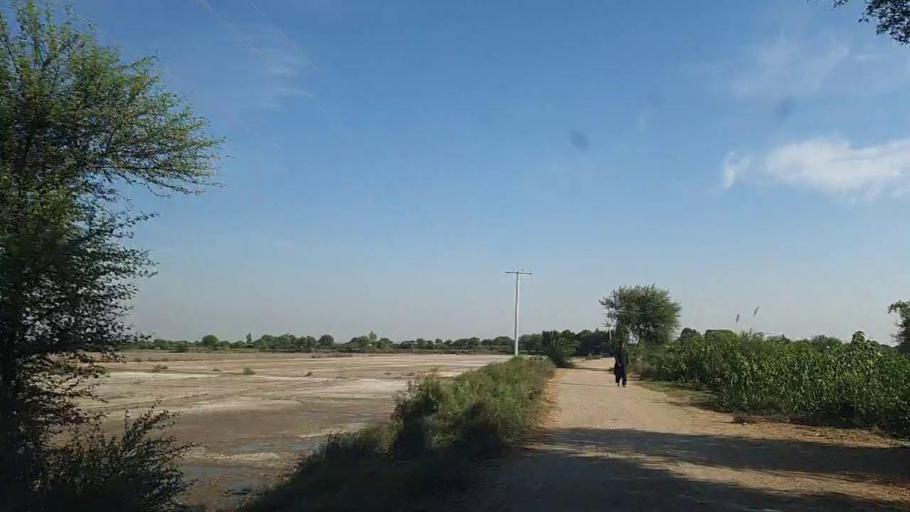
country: PK
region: Sindh
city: Bulri
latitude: 24.7770
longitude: 68.3596
